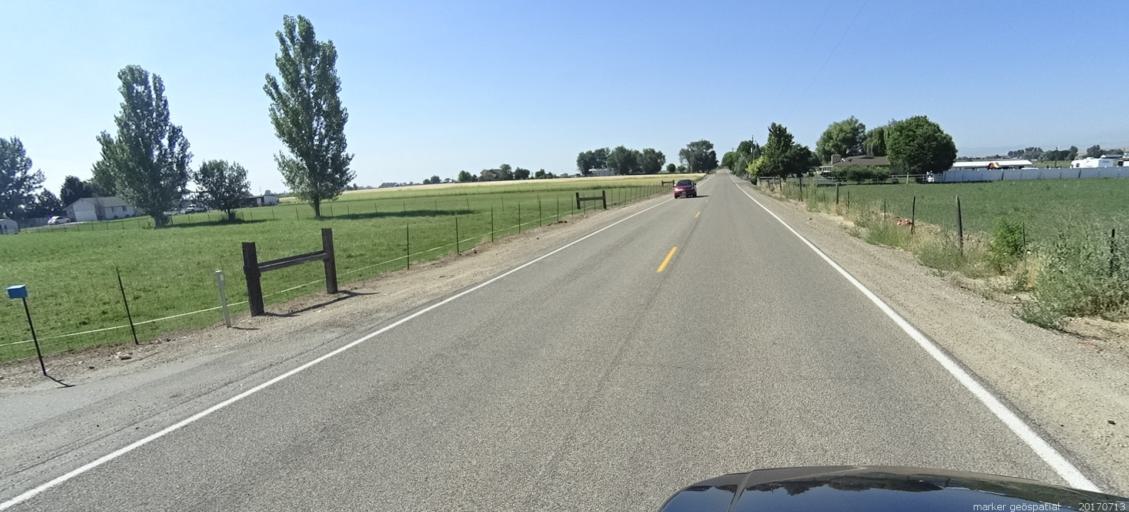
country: US
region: Idaho
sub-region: Ada County
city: Kuna
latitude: 43.5100
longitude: -116.3743
